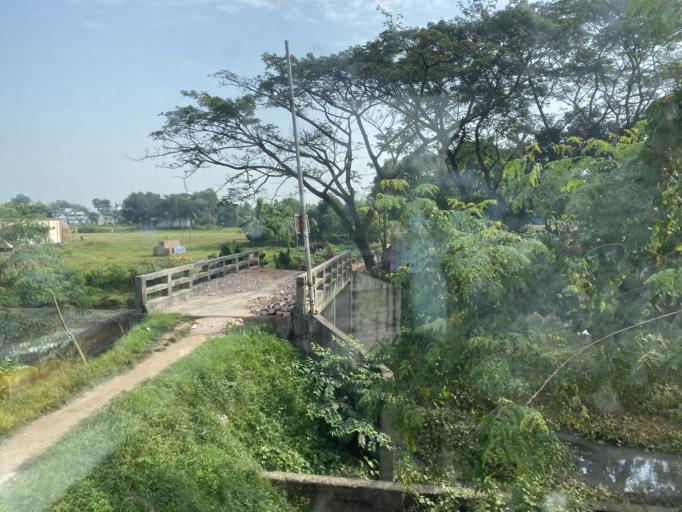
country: BD
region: Chittagong
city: Nabinagar
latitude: 23.9593
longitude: 91.1193
